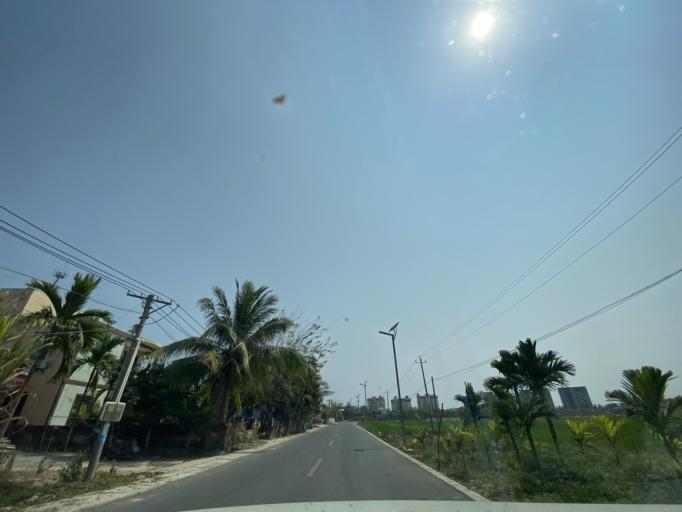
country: CN
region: Hainan
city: Yingzhou
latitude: 18.4101
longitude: 109.8152
